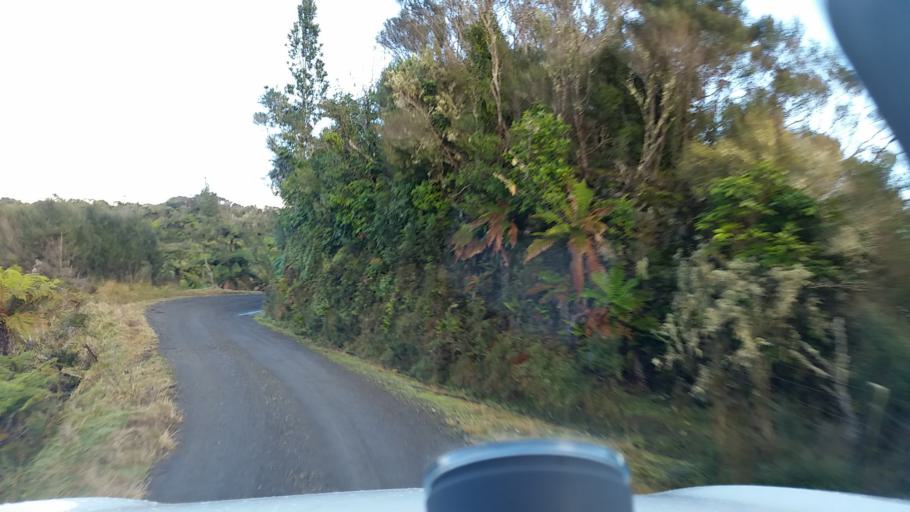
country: NZ
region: Taranaki
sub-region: South Taranaki District
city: Eltham
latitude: -39.4173
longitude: 174.5581
